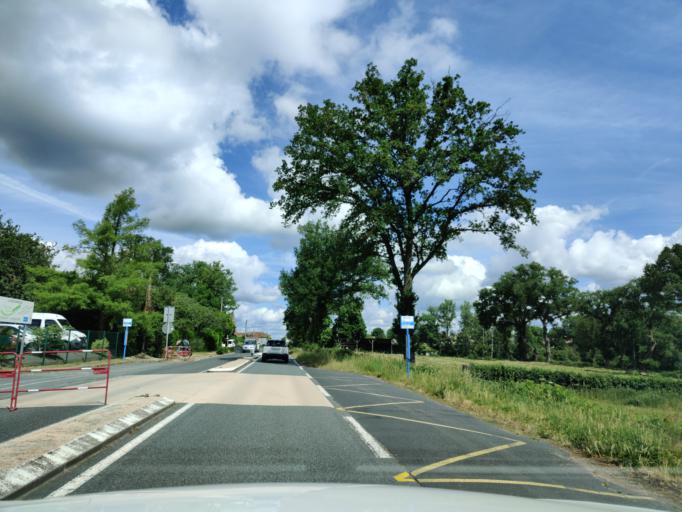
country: FR
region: Auvergne
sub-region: Departement de l'Allier
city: Durdat-Larequille
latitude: 46.2476
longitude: 2.7040
